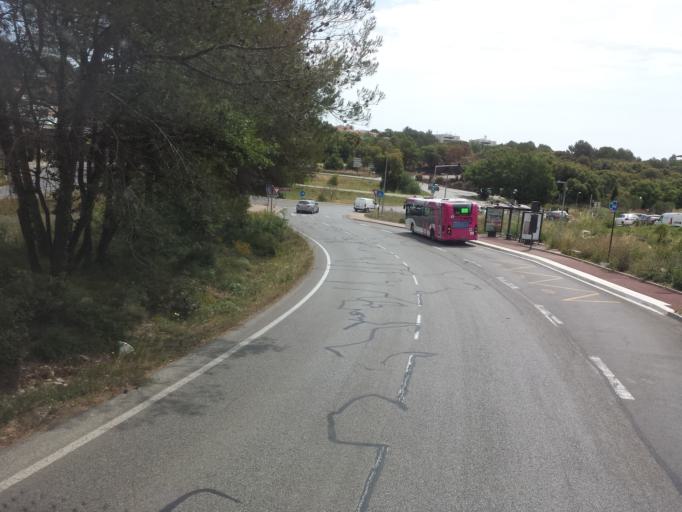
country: FR
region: Provence-Alpes-Cote d'Azur
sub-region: Departement des Alpes-Maritimes
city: Biot
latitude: 43.6170
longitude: 7.0725
